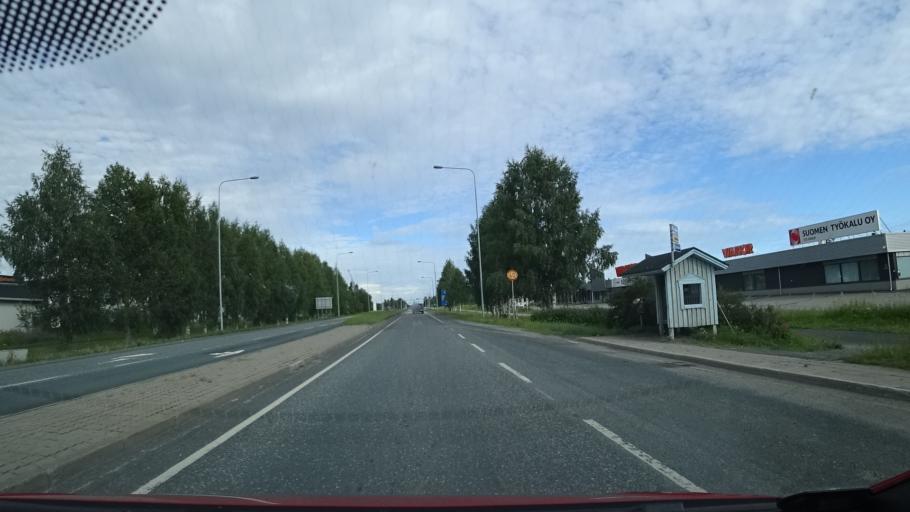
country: FI
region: Lapland
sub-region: Kemi-Tornio
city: Keminmaa
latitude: 65.7992
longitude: 24.5064
